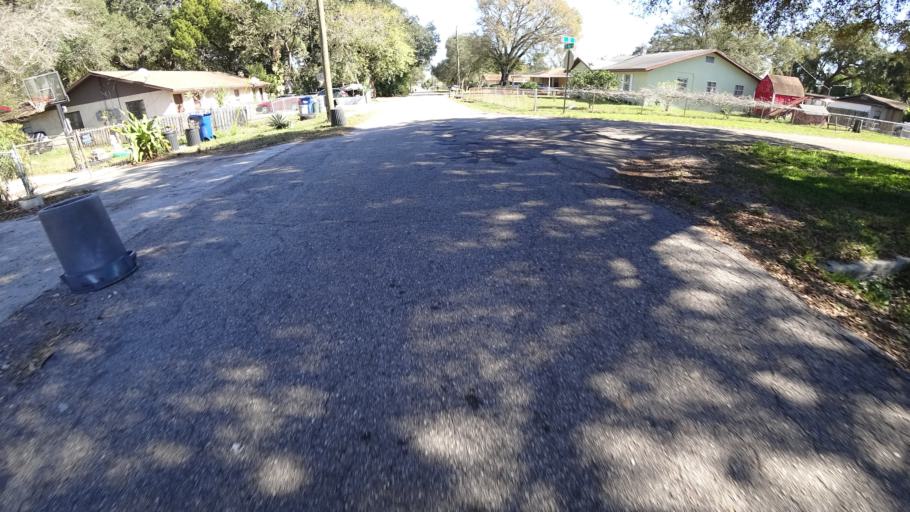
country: US
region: Florida
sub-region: Manatee County
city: West Samoset
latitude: 27.4789
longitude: -82.5580
